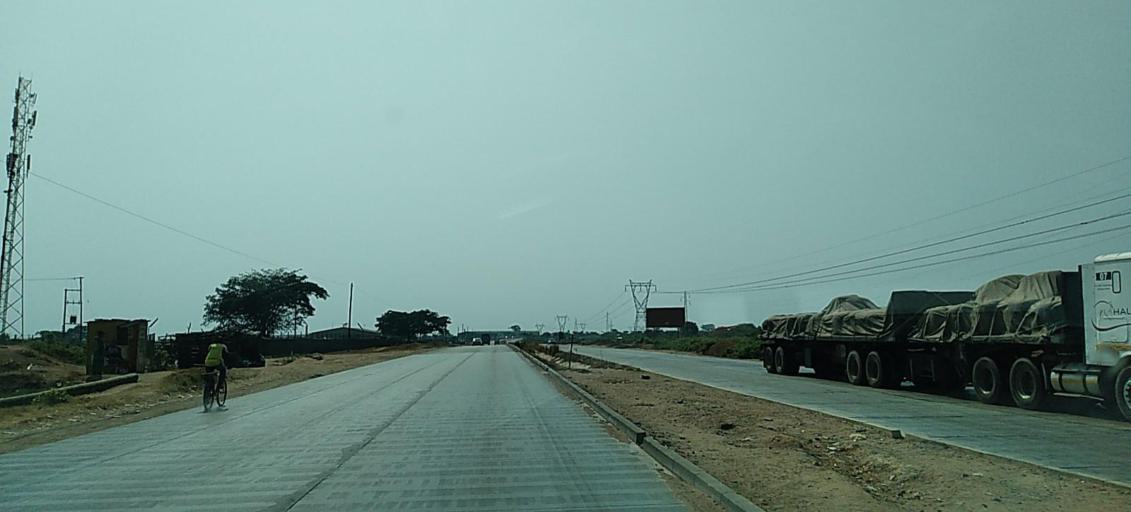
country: ZM
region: Copperbelt
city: Chingola
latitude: -12.5670
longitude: 27.8989
